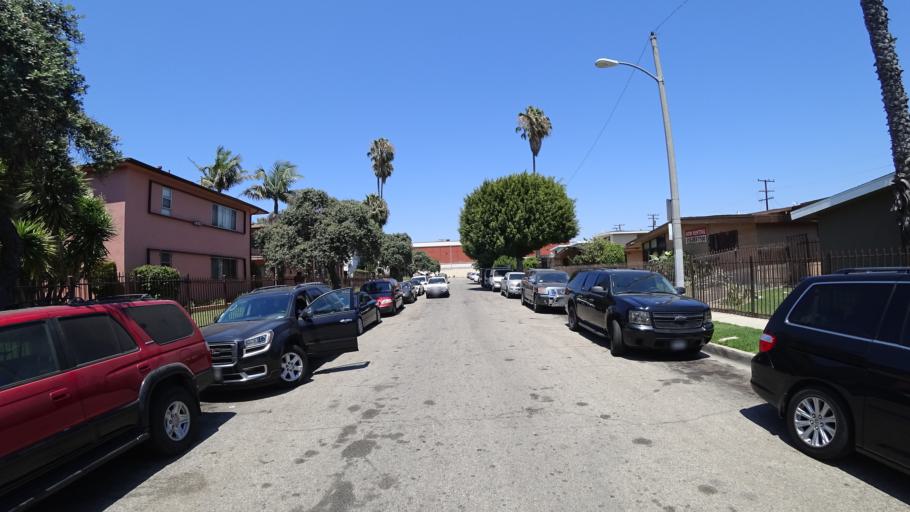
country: US
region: California
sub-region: Los Angeles County
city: Lennox
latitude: 33.9427
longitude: -118.3277
